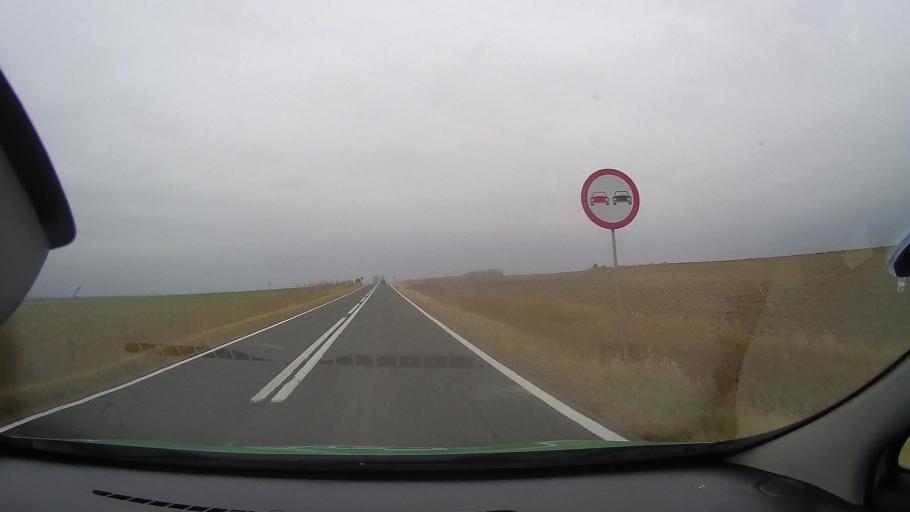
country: RO
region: Constanta
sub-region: Comuna Ciobanu
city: Ciobanu
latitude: 44.7006
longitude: 28.0121
